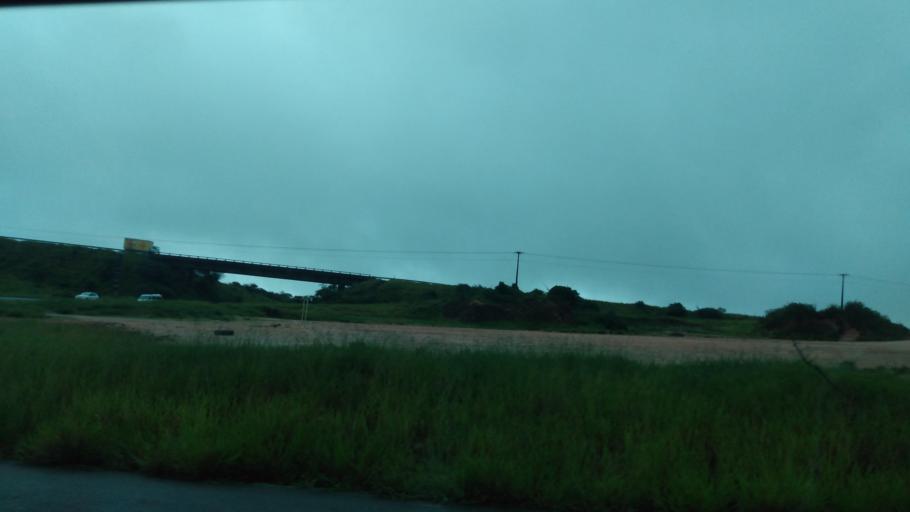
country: BR
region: Pernambuco
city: Garanhuns
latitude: -8.8781
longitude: -36.5065
